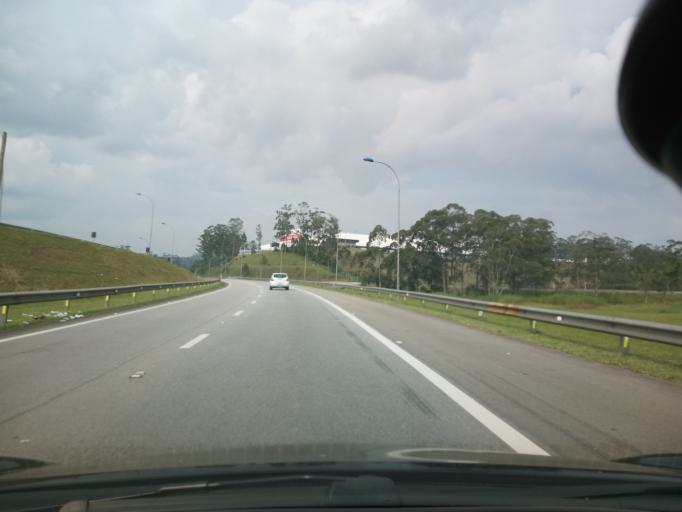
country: BR
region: Sao Paulo
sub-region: Sao Bernardo Do Campo
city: Sao Bernardo do Campo
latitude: -23.7657
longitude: -46.5903
